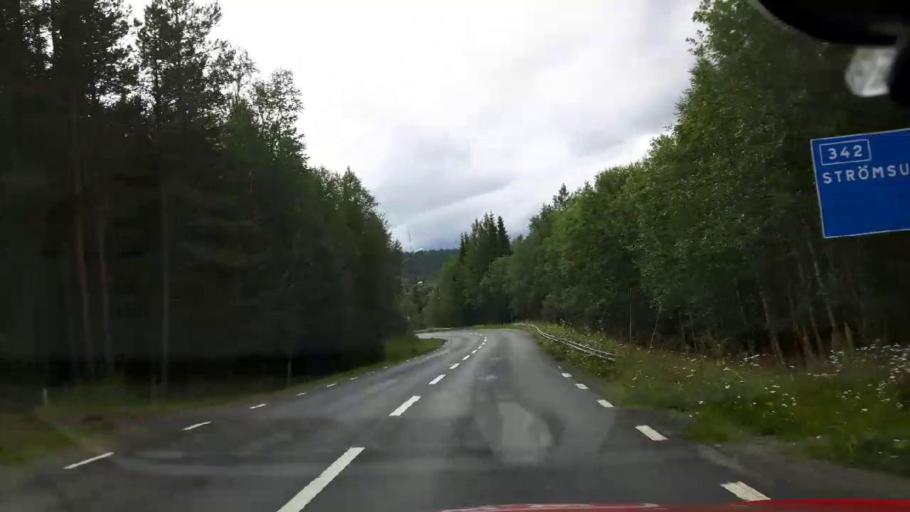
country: NO
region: Nord-Trondelag
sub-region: Lierne
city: Sandvika
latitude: 64.5005
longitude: 14.1533
